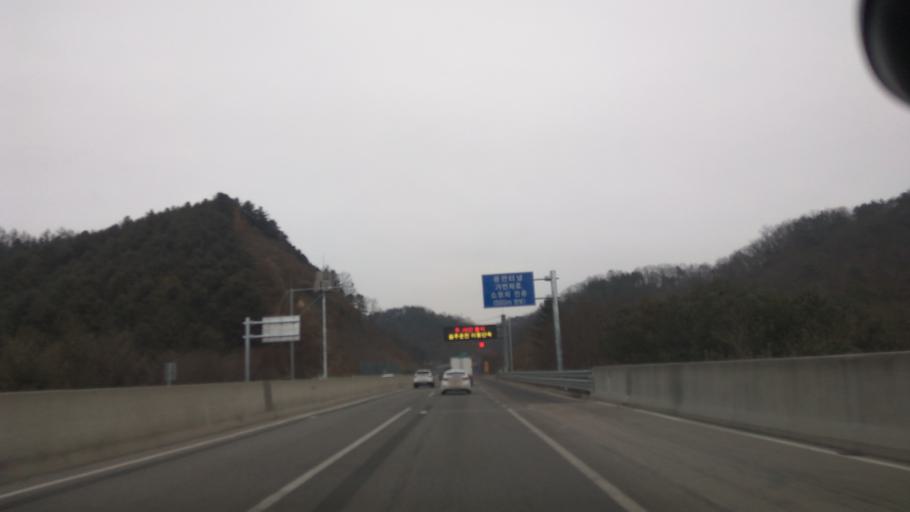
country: KR
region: Gangwon-do
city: Sindong
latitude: 37.7448
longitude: 127.6933
